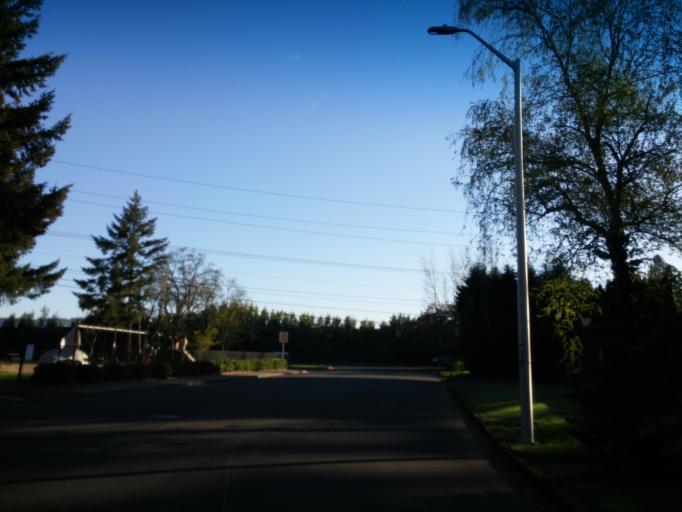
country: US
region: Oregon
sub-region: Washington County
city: Cedar Hills
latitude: 45.5119
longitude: -122.7916
